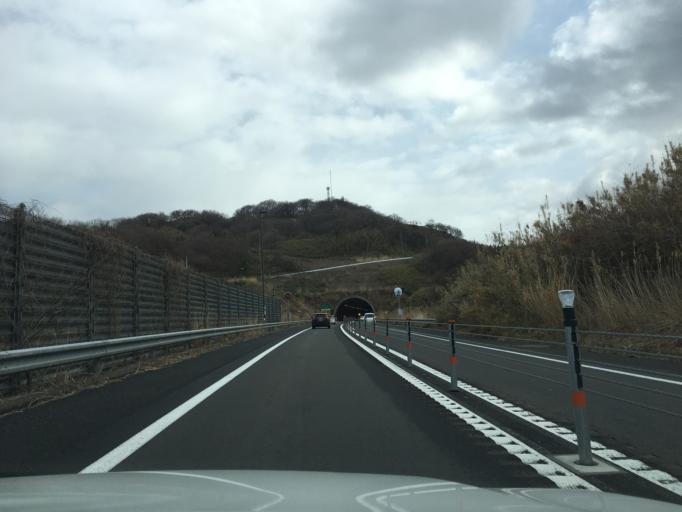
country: JP
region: Yamagata
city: Yuza
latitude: 39.3163
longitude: 139.9892
